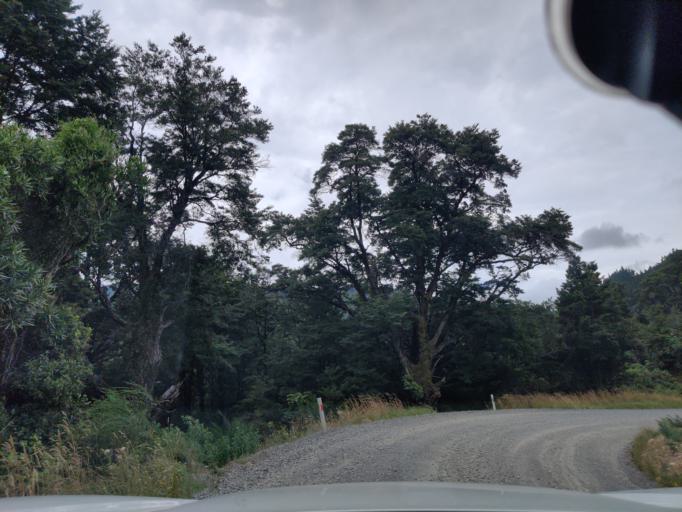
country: NZ
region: Wellington
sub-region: Masterton District
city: Masterton
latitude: -41.0403
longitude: 175.4036
